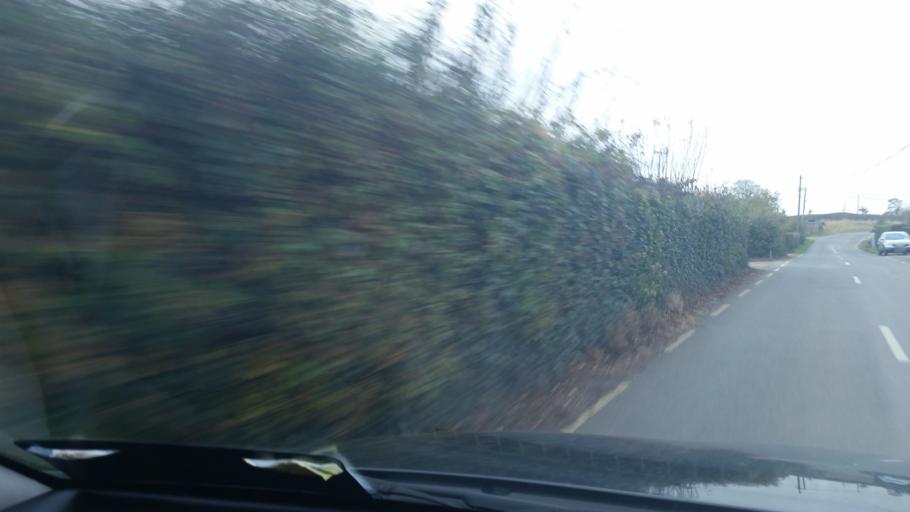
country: IE
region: Leinster
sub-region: Lu
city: Tullyallen
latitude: 53.6977
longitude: -6.4107
